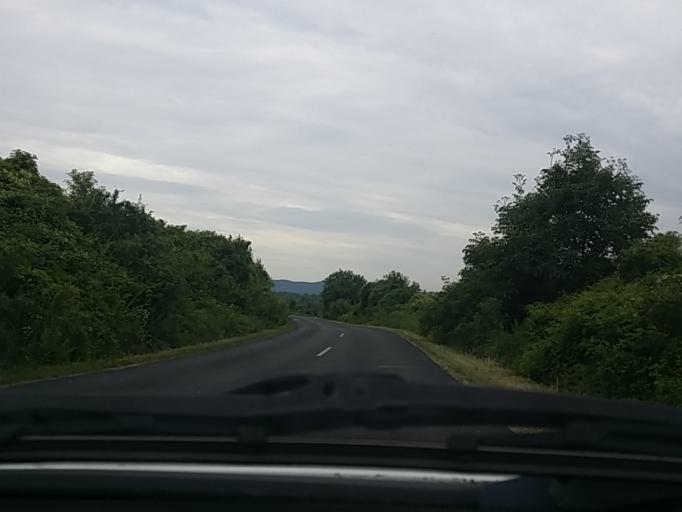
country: HU
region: Pest
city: Csobanka
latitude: 47.6354
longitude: 18.9548
